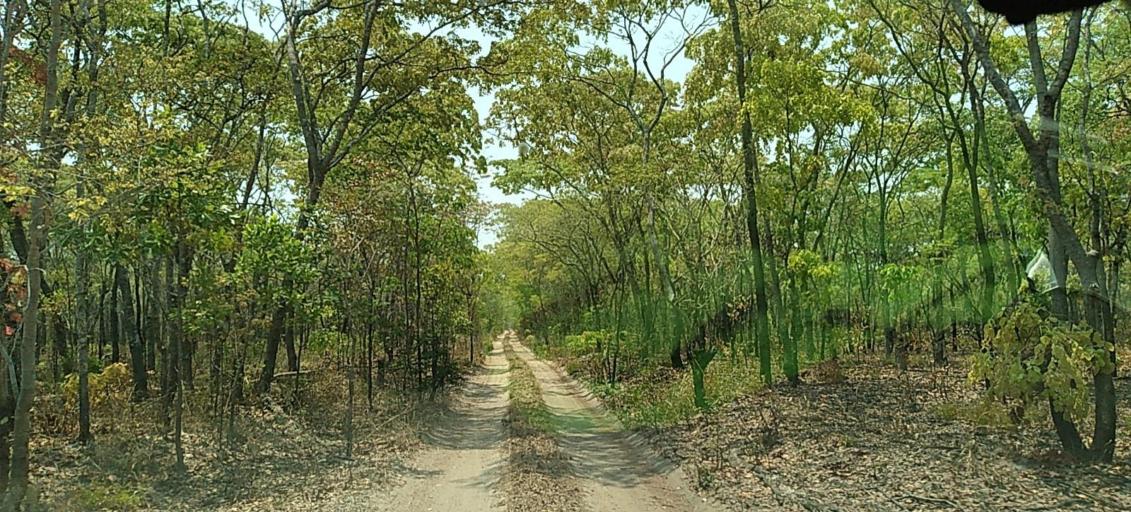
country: ZM
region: North-Western
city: Kabompo
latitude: -13.6527
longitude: 24.4703
